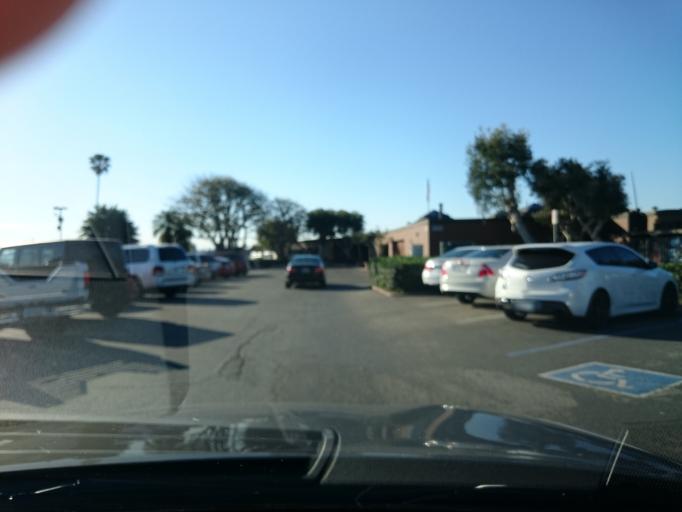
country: US
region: California
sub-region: San Diego County
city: La Jolla
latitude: 32.7825
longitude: -117.2492
